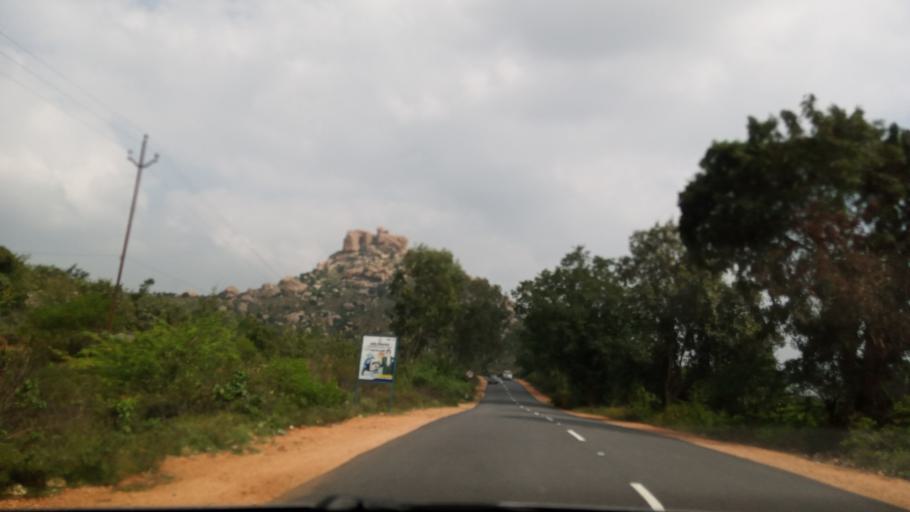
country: IN
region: Andhra Pradesh
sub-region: Chittoor
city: Madanapalle
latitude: 13.6357
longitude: 78.6112
